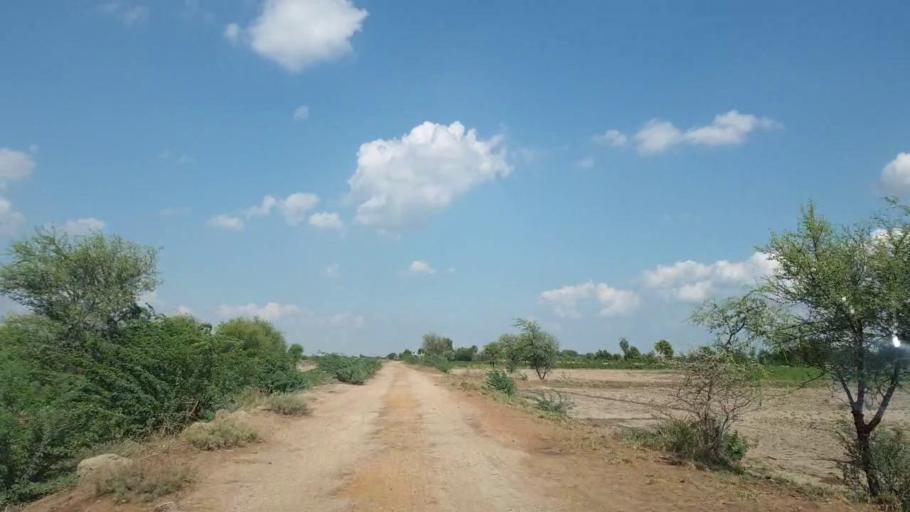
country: PK
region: Sindh
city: Pithoro
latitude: 25.6009
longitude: 69.3886
